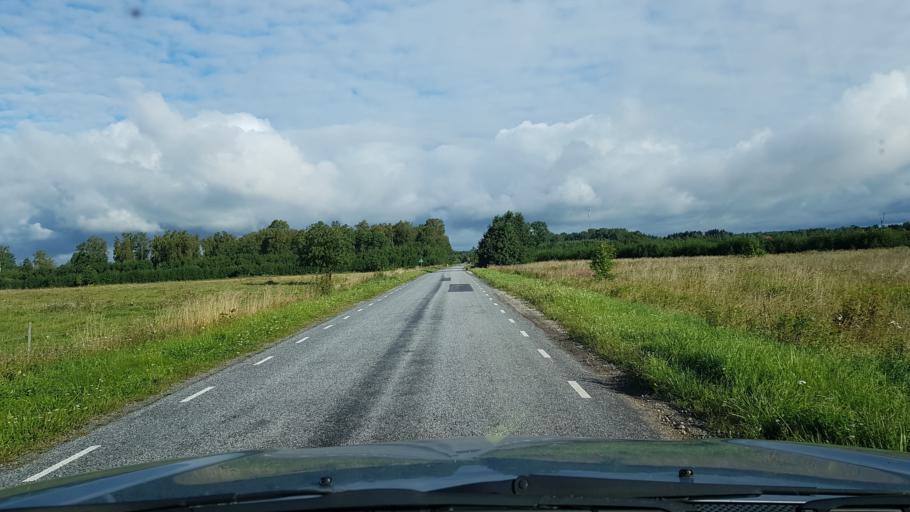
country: EE
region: Harju
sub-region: Rae vald
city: Vaida
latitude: 59.3054
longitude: 24.9266
